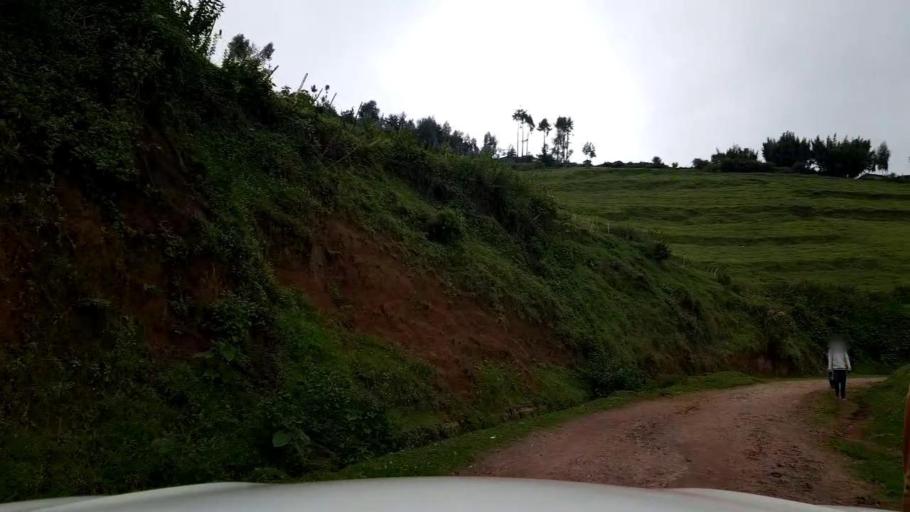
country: RW
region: Western Province
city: Gisenyi
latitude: -1.6746
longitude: 29.4128
